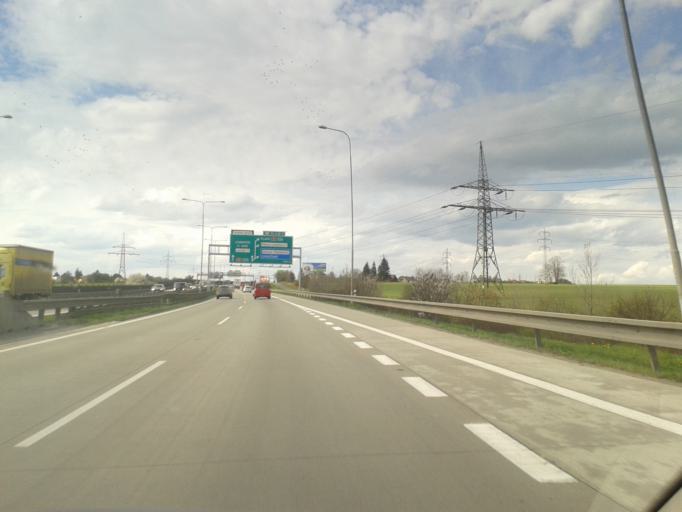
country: CZ
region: Central Bohemia
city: Rudna
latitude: 50.0329
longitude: 14.2810
